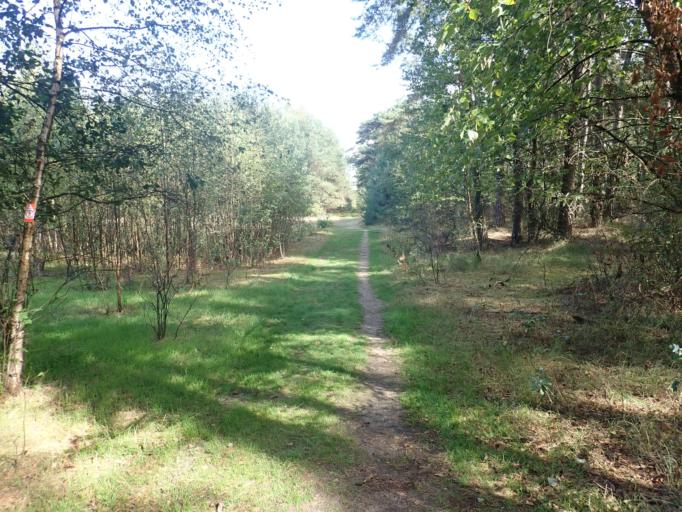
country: BE
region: Flanders
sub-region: Provincie Antwerpen
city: Rijkevorsel
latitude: 51.3153
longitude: 4.7977
